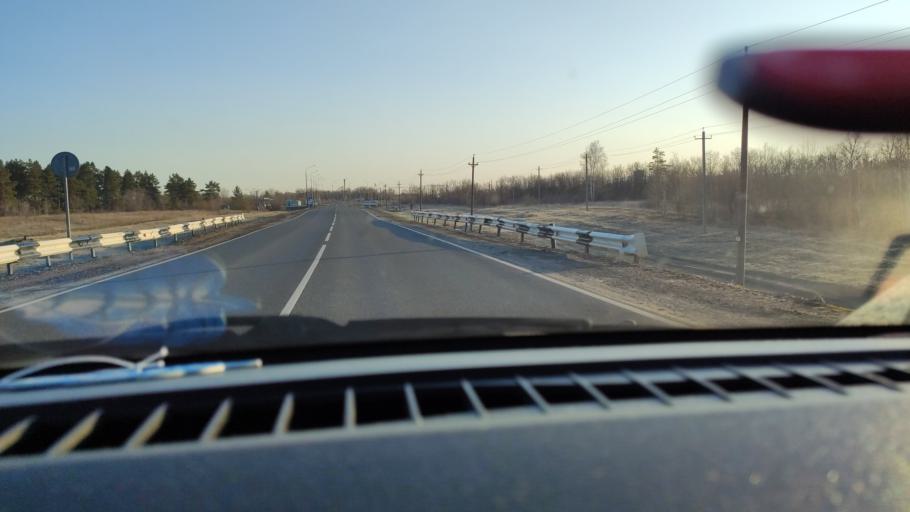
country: RU
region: Saratov
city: Sennoy
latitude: 52.1481
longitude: 46.9467
